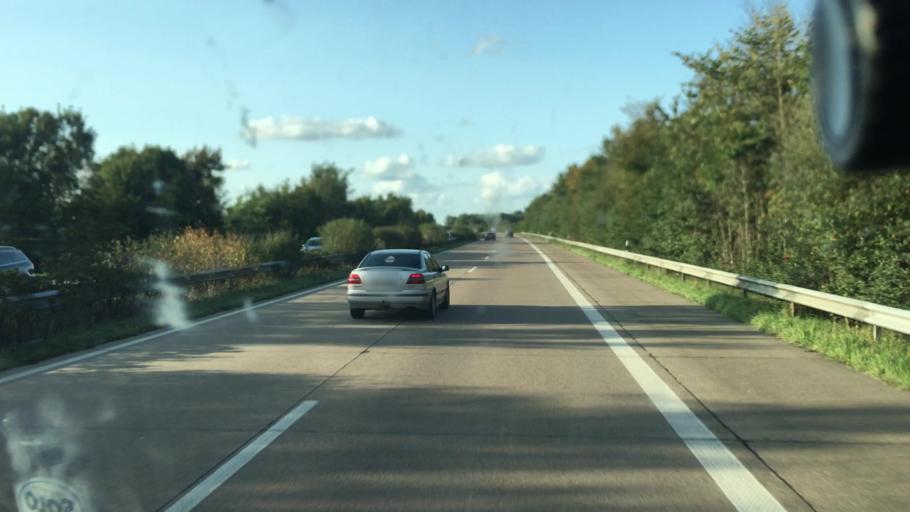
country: DE
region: Lower Saxony
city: Sande
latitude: 53.4660
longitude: 8.0174
